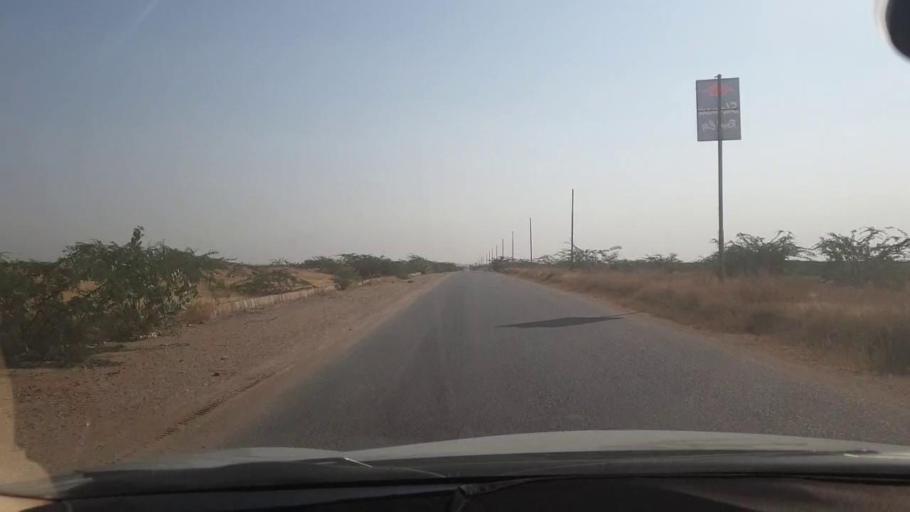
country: PK
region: Sindh
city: Malir Cantonment
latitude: 25.0682
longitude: 67.1388
